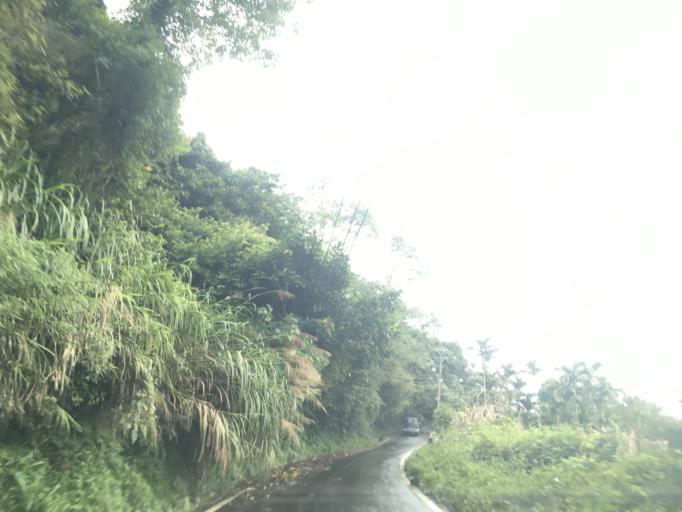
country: TW
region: Taiwan
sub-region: Yunlin
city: Douliu
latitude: 23.5642
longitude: 120.6588
